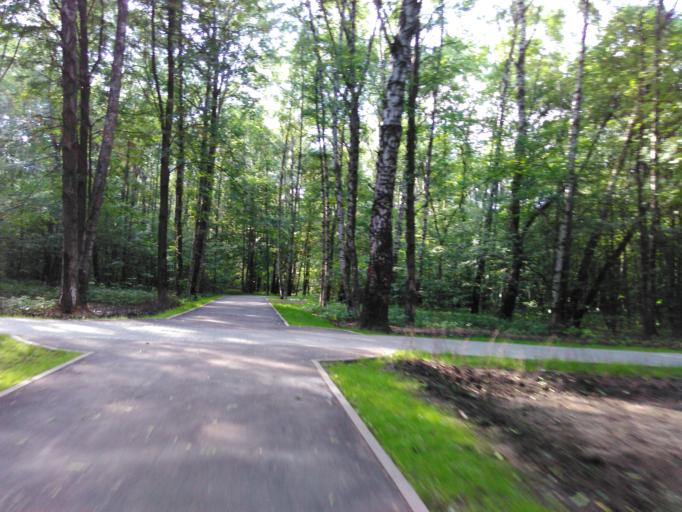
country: RU
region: Moscow
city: Troparevo
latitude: 55.6551
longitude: 37.5111
